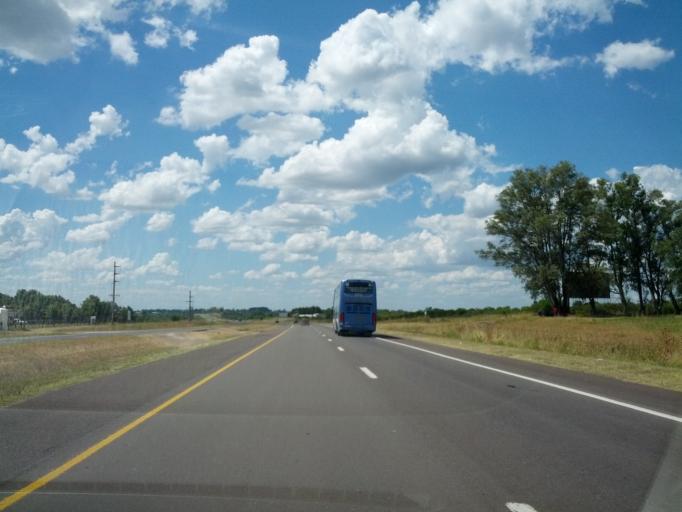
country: AR
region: Entre Rios
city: Concepcion del Uruguay
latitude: -32.4312
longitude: -58.2848
